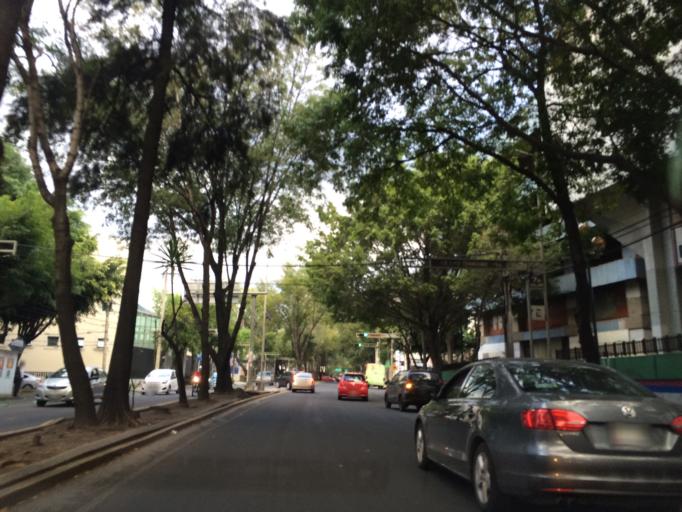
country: MX
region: Mexico City
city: Colonia del Valle
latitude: 19.3672
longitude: -99.1589
